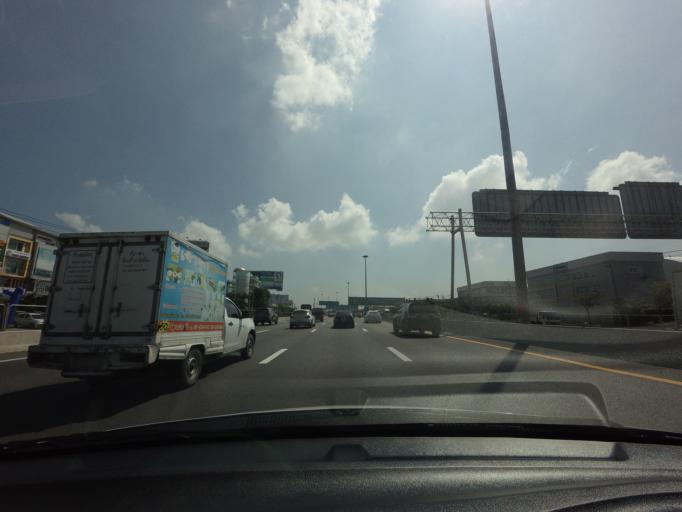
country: TH
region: Bangkok
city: Lat Krabang
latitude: 13.7295
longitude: 100.7321
